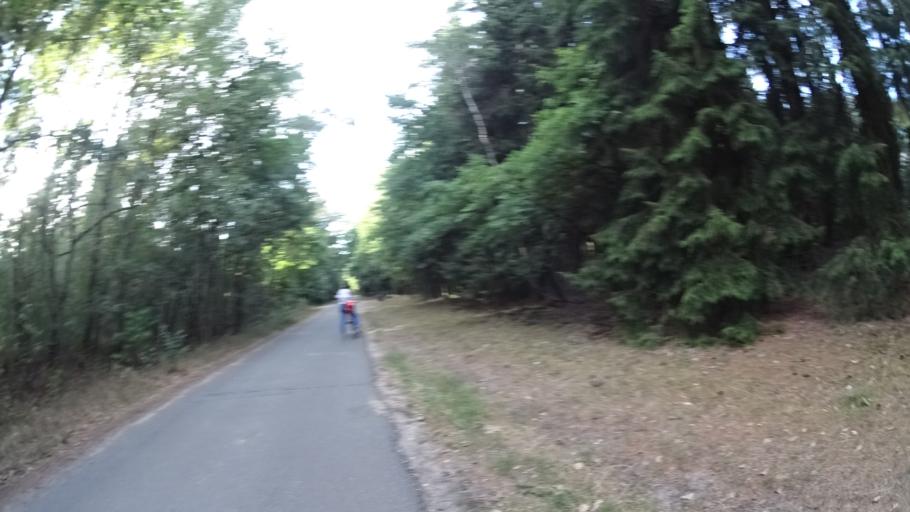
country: DE
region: Lower Saxony
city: Handeloh
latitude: 53.2356
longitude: 9.8660
